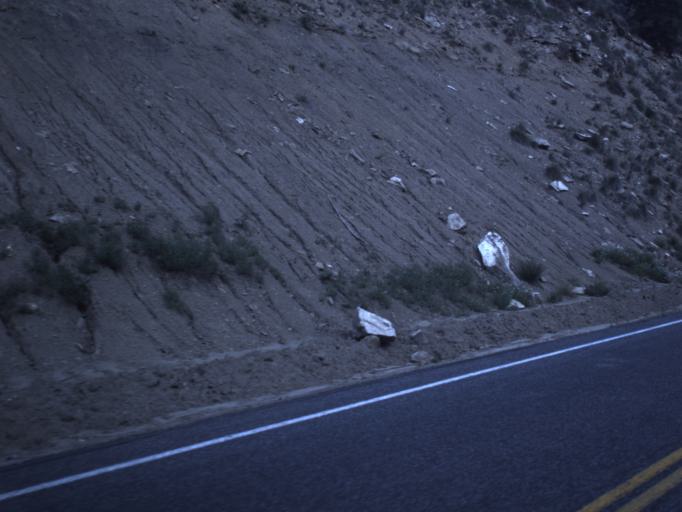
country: US
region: Utah
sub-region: Emery County
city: Huntington
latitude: 39.4832
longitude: -111.1587
